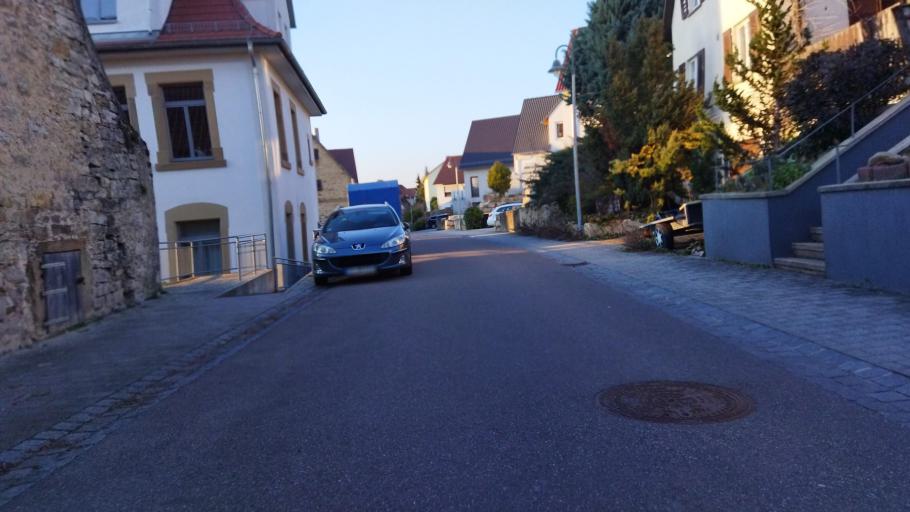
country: DE
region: Baden-Wuerttemberg
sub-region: Regierungsbezirk Stuttgart
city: Gemmrigheim
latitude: 49.0237
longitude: 9.1578
